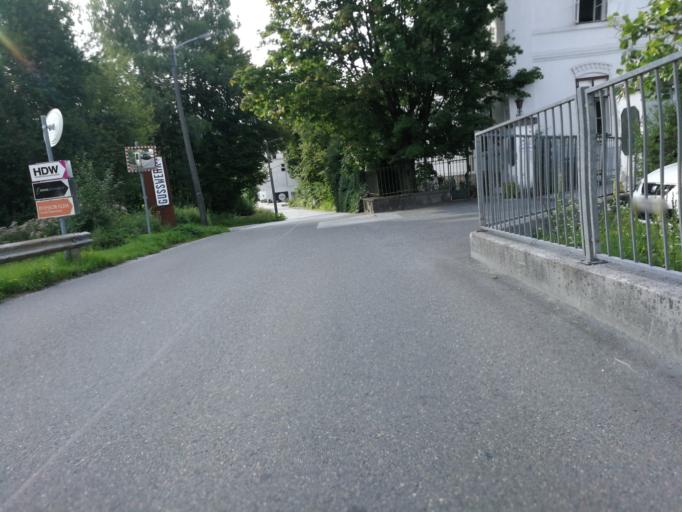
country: AT
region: Salzburg
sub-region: Politischer Bezirk Salzburg-Umgebung
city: Hallwang
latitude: 47.8372
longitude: 13.0629
